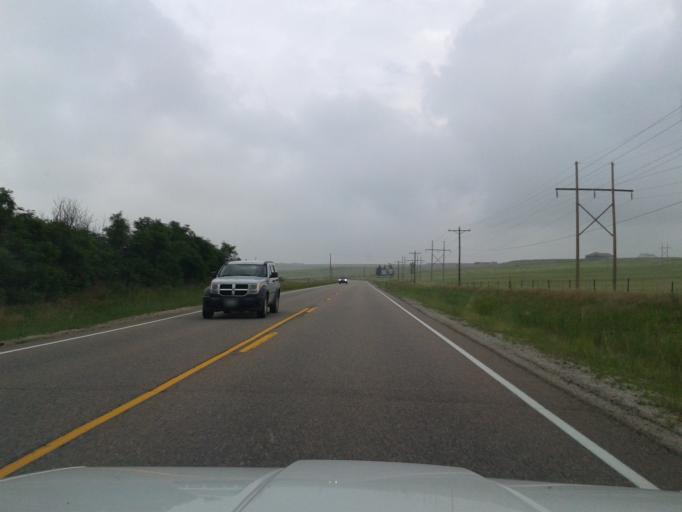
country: US
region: Colorado
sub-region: Elbert County
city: Elizabeth
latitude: 39.2319
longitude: -104.6979
